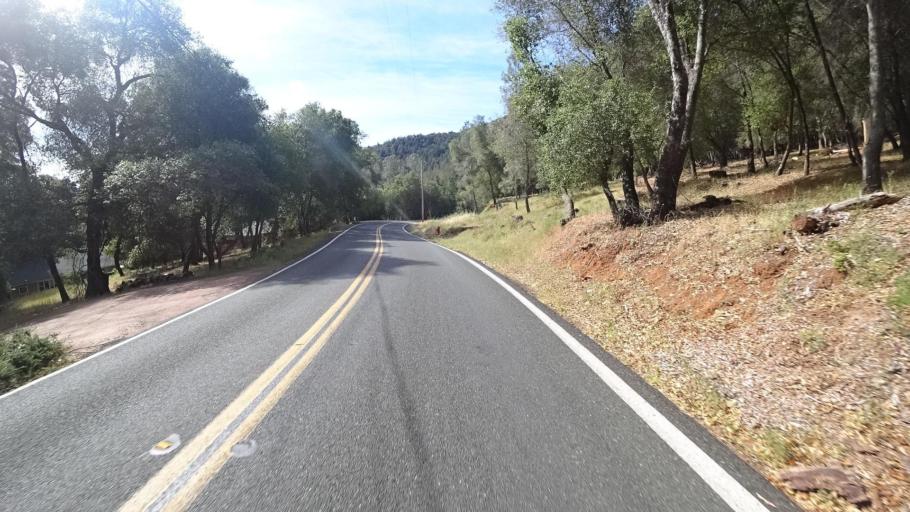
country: US
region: California
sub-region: Lake County
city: Soda Bay
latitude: 39.0027
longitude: -122.7623
